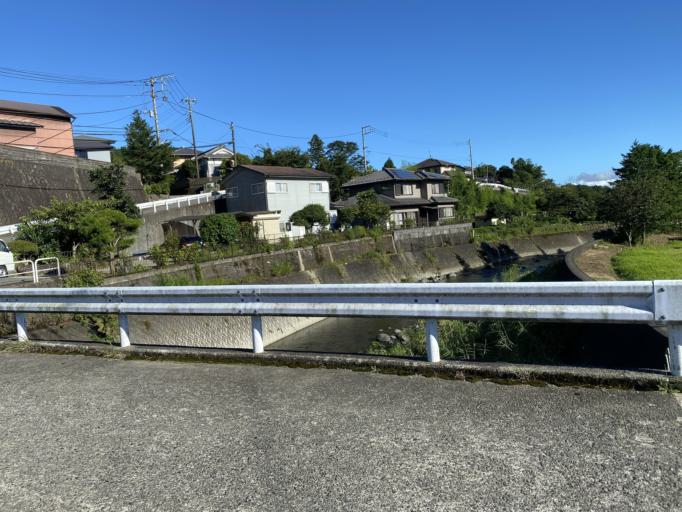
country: BR
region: Paraiba
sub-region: Imaculada
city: Imaculada
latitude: -7.3930
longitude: -37.5929
